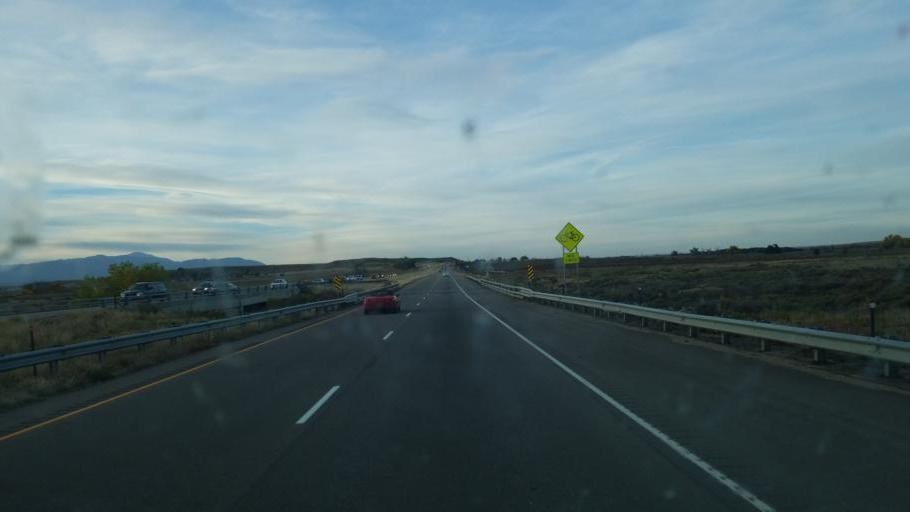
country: US
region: Colorado
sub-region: Pueblo County
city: Pueblo West
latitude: 38.4877
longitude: -104.6207
